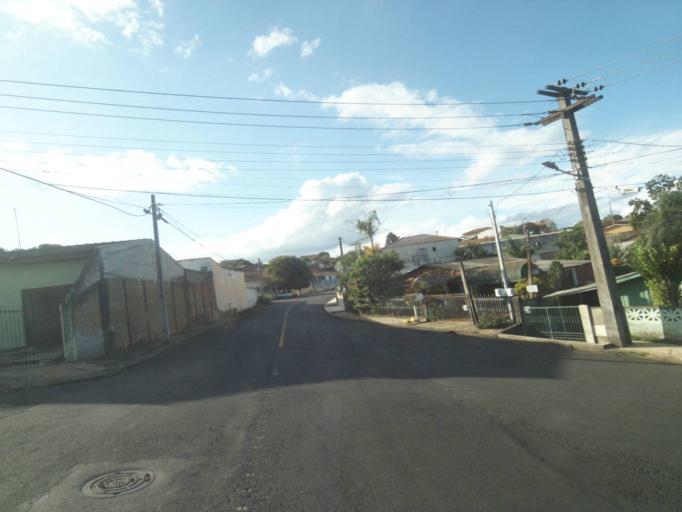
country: BR
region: Parana
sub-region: Telemaco Borba
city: Telemaco Borba
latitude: -24.3381
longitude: -50.6206
